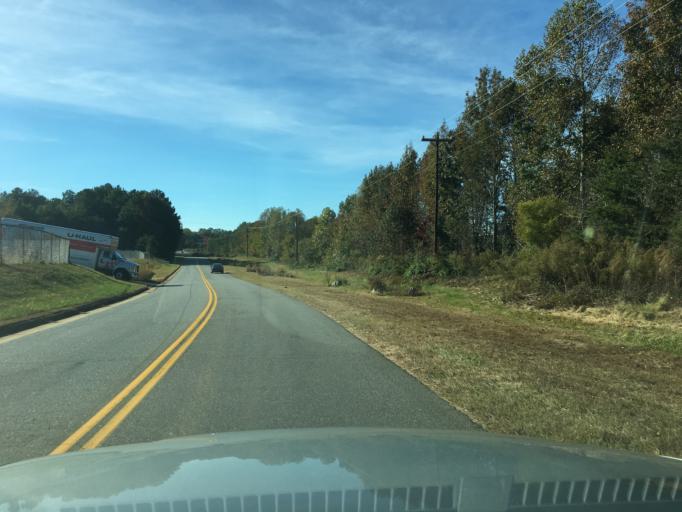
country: US
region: North Carolina
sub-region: Catawba County
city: Saint Stephens
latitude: 35.7044
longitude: -81.2853
